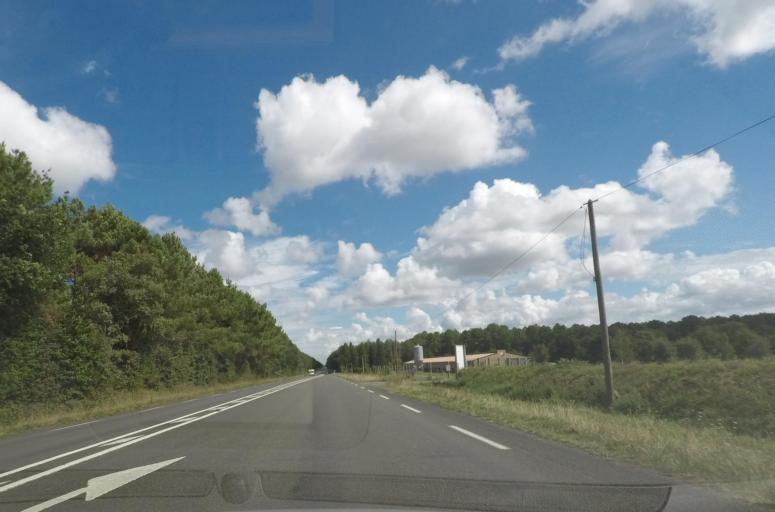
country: FR
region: Pays de la Loire
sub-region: Departement de la Sarthe
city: Mezeray
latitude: 47.7771
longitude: 0.0294
